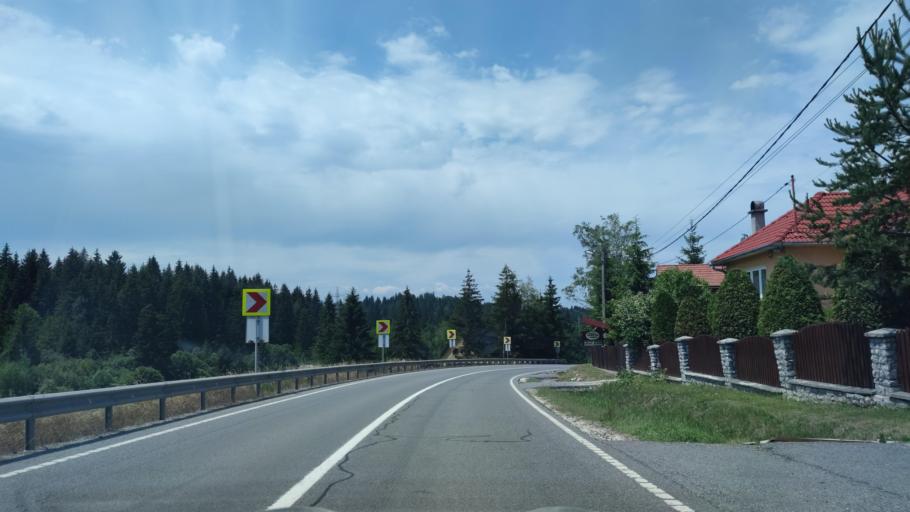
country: RO
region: Harghita
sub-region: Comuna Voslobeni
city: Voslobeni
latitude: 46.6193
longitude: 25.6951
